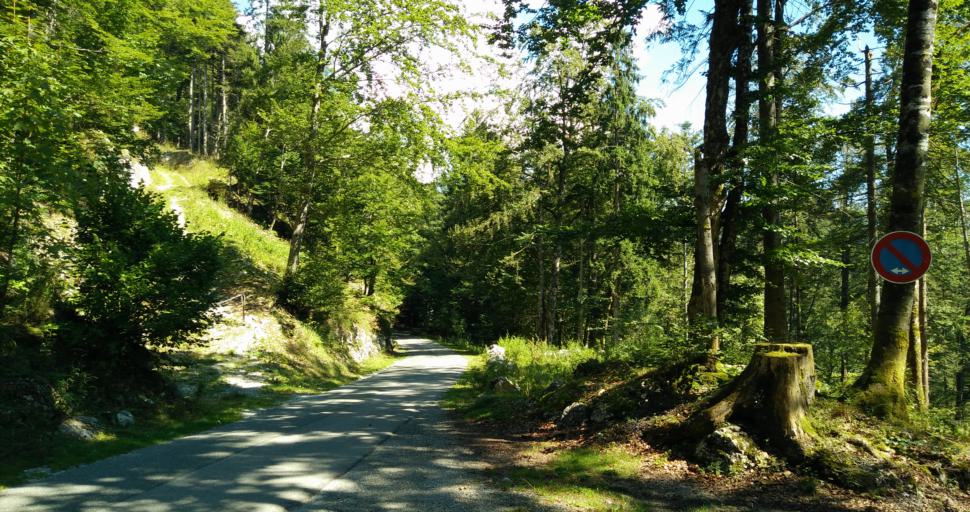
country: AT
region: Salzburg
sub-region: Politischer Bezirk Hallein
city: Scheffau am Tennengebirge
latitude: 47.6310
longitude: 13.2357
